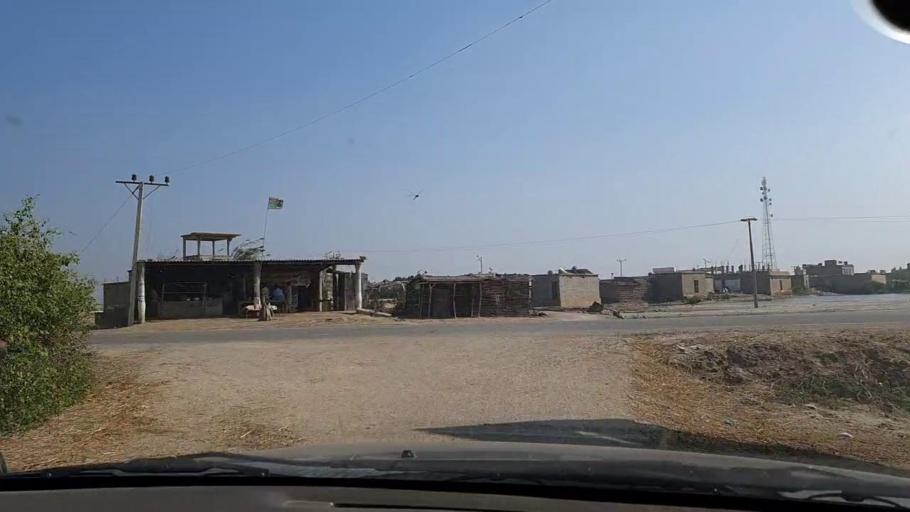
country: PK
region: Sindh
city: Chuhar Jamali
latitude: 24.3951
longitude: 67.8249
